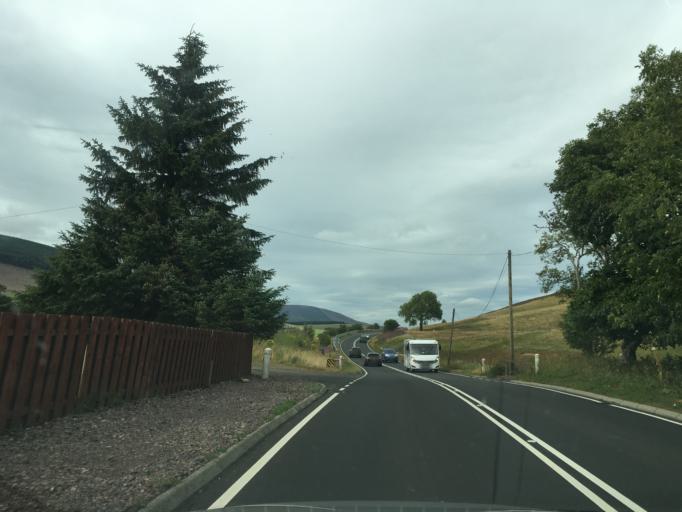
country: GB
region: Scotland
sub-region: South Lanarkshire
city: Biggar
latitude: 55.5345
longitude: -3.6657
